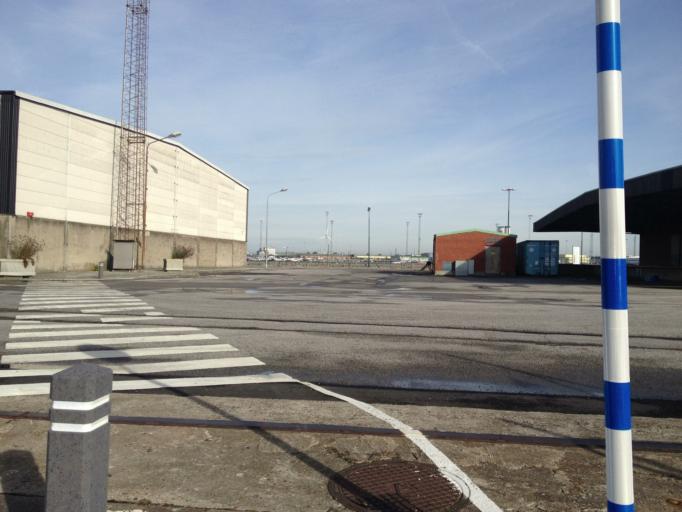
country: SE
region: Skane
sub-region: Malmo
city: Malmoe
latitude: 55.6145
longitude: 13.0035
